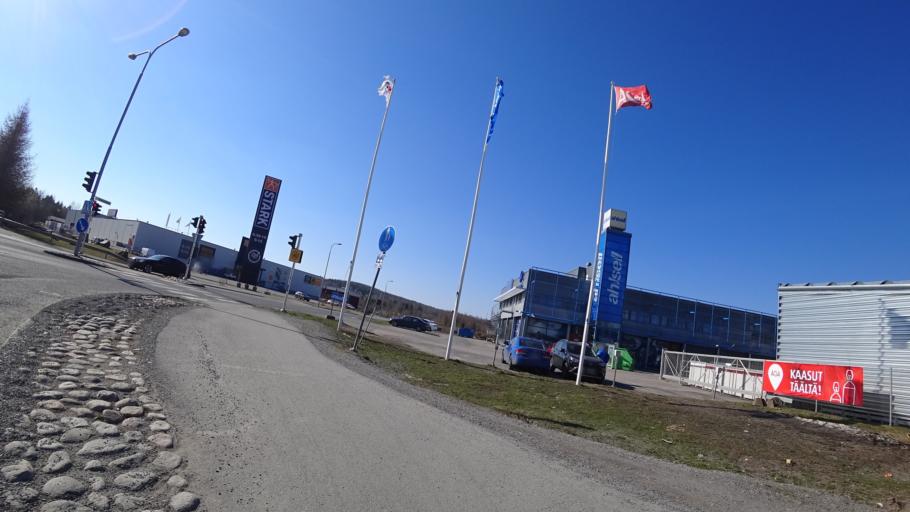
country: FI
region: Pirkanmaa
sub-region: Tampere
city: Pirkkala
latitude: 61.5219
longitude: 23.6544
